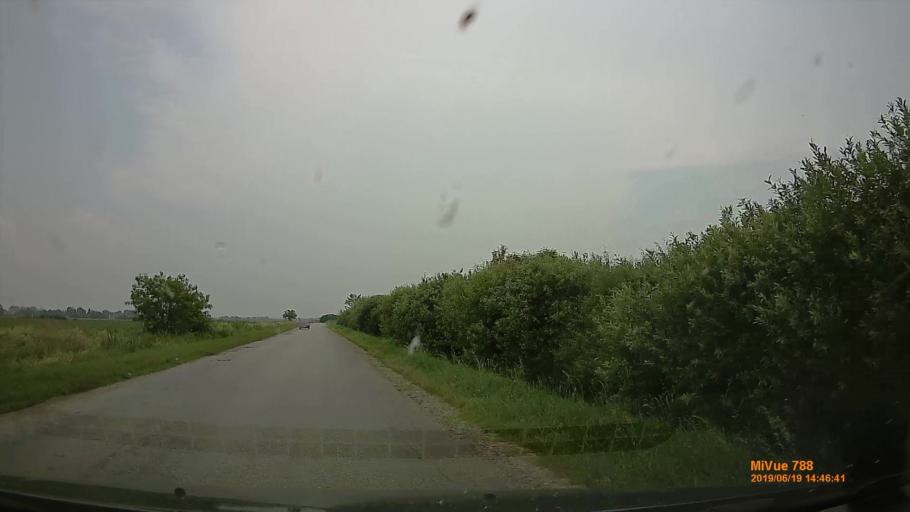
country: HU
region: Baranya
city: Szigetvar
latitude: 46.0035
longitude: 17.8252
